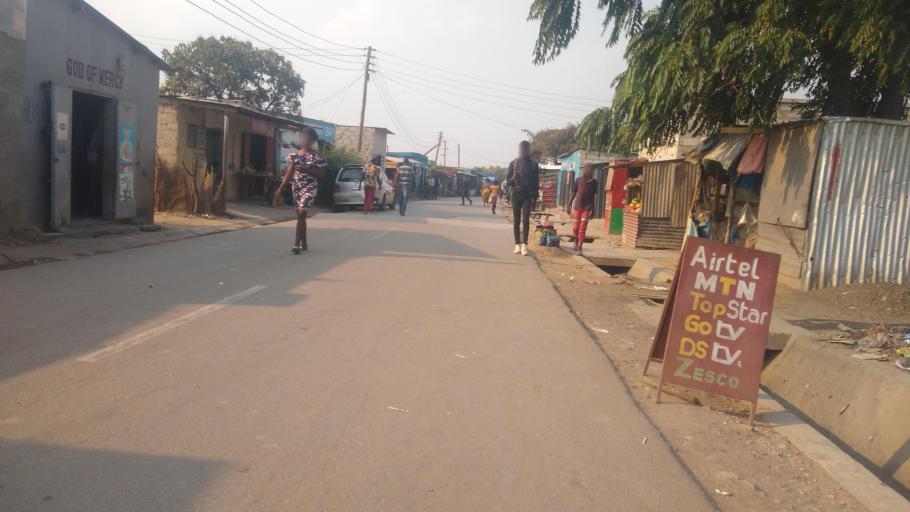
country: ZM
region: Lusaka
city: Lusaka
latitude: -15.4448
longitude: 28.3800
